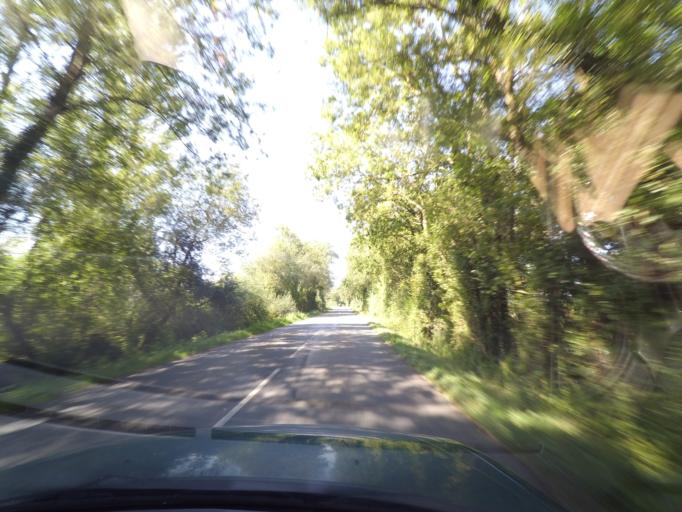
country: FR
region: Pays de la Loire
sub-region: Departement de la Loire-Atlantique
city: Saint-Lumine-de-Coutais
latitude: 47.0380
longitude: -1.6986
